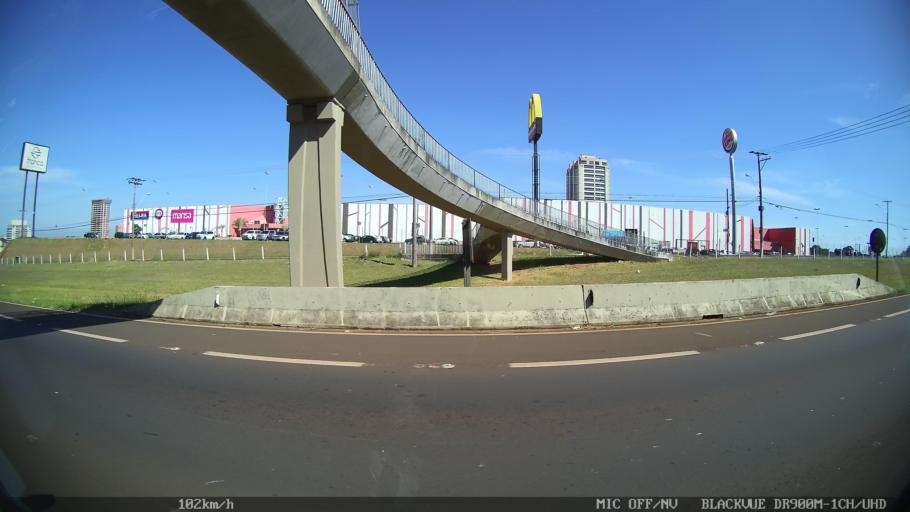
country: BR
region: Sao Paulo
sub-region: Franca
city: Franca
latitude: -20.5468
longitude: -47.4157
